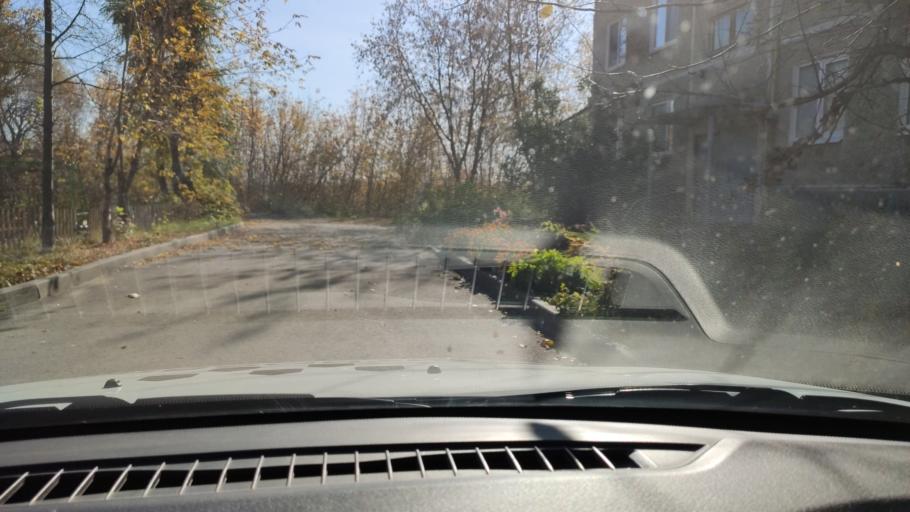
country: RU
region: Perm
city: Kondratovo
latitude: 57.9500
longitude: 56.1160
